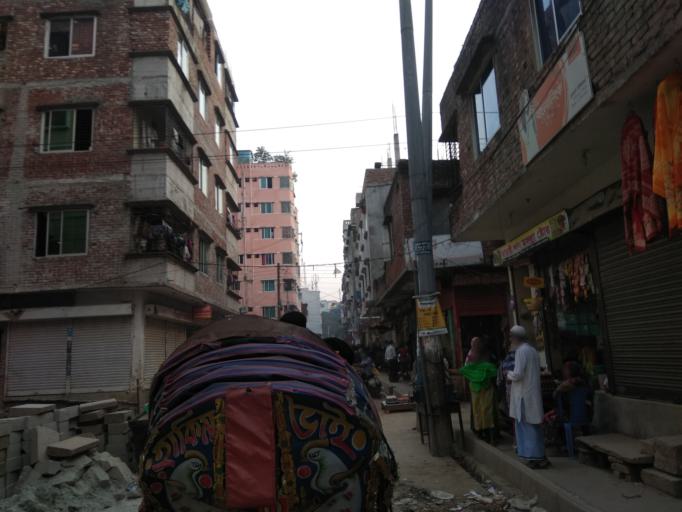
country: BD
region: Dhaka
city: Tungi
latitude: 23.8171
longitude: 90.3640
